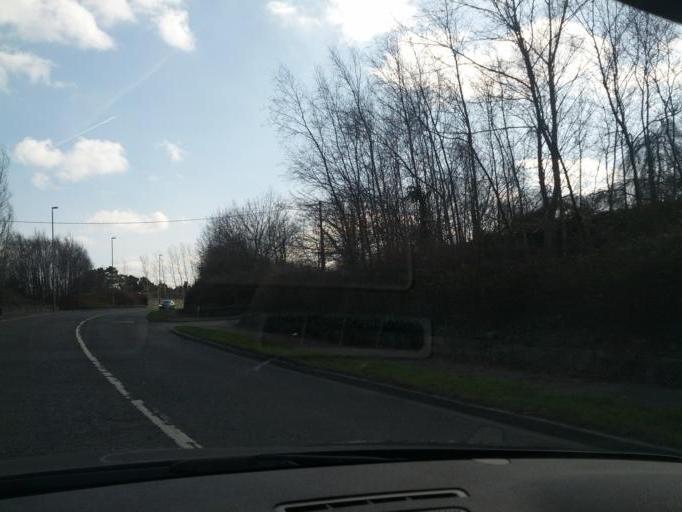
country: IE
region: Leinster
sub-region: Kildare
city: Leixlip
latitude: 53.3477
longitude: -6.5090
